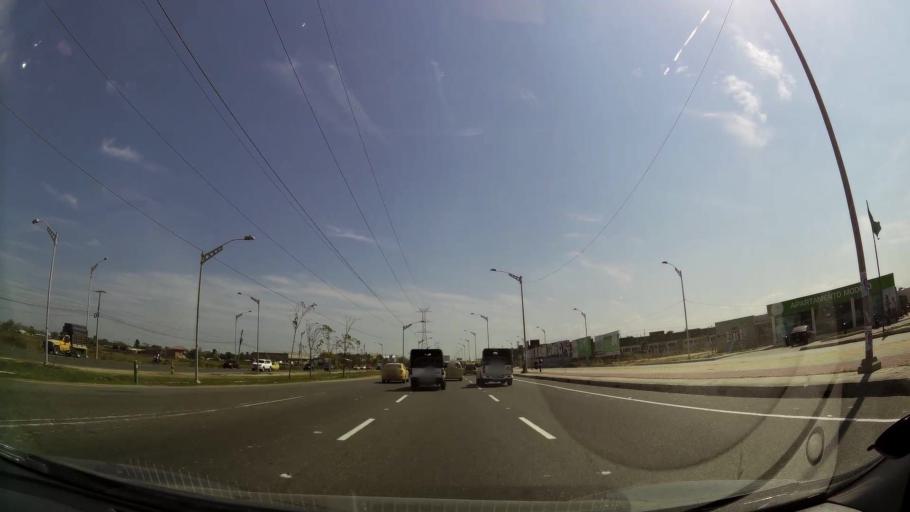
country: CO
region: Atlantico
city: Barranquilla
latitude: 10.9585
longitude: -74.8369
